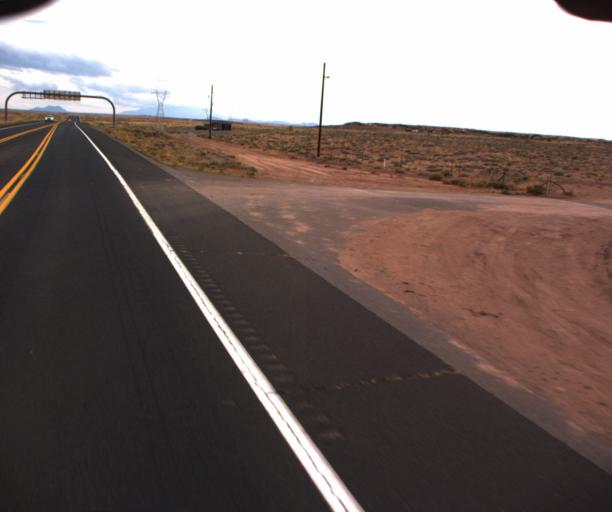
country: US
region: Arizona
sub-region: Coconino County
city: Tuba City
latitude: 35.8230
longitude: -111.4402
